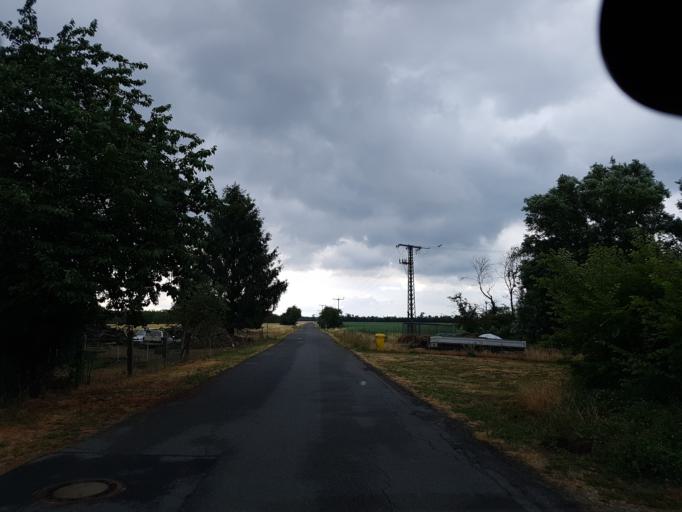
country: DE
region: Saxony-Anhalt
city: Seyda
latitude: 51.9243
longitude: 12.9199
